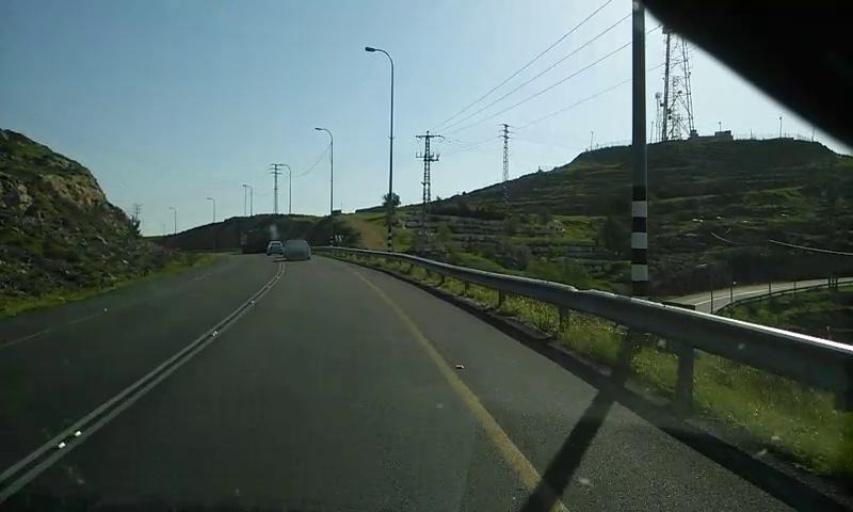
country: PS
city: Al Buq`ah
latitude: 31.5274
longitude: 35.1298
